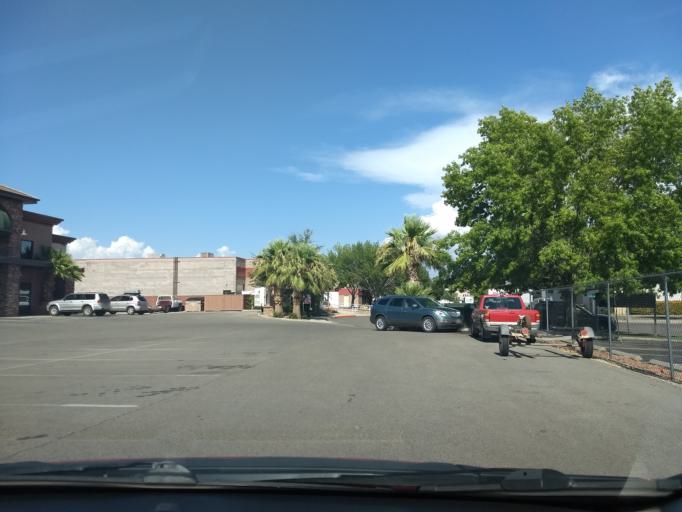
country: US
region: Utah
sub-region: Washington County
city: Saint George
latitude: 37.0845
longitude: -113.5787
